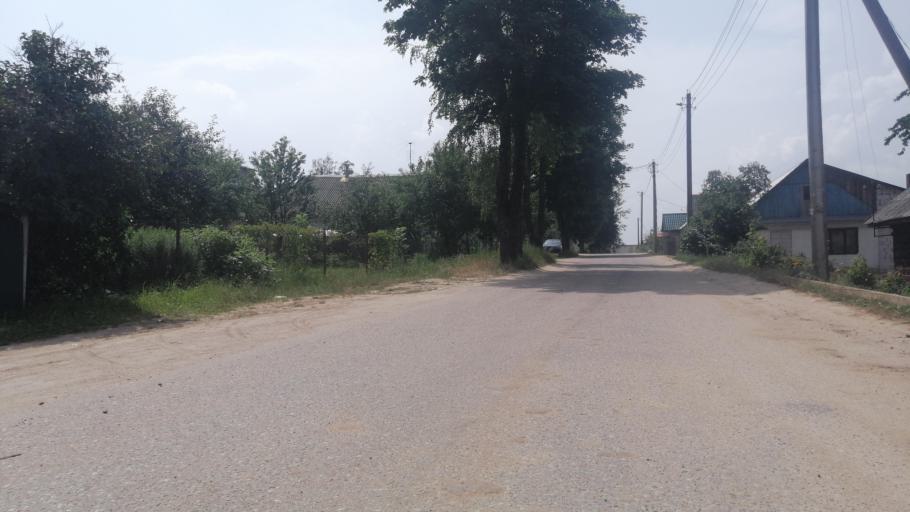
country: BY
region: Grodnenskaya
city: Navahrudak
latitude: 53.6044
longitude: 25.8259
